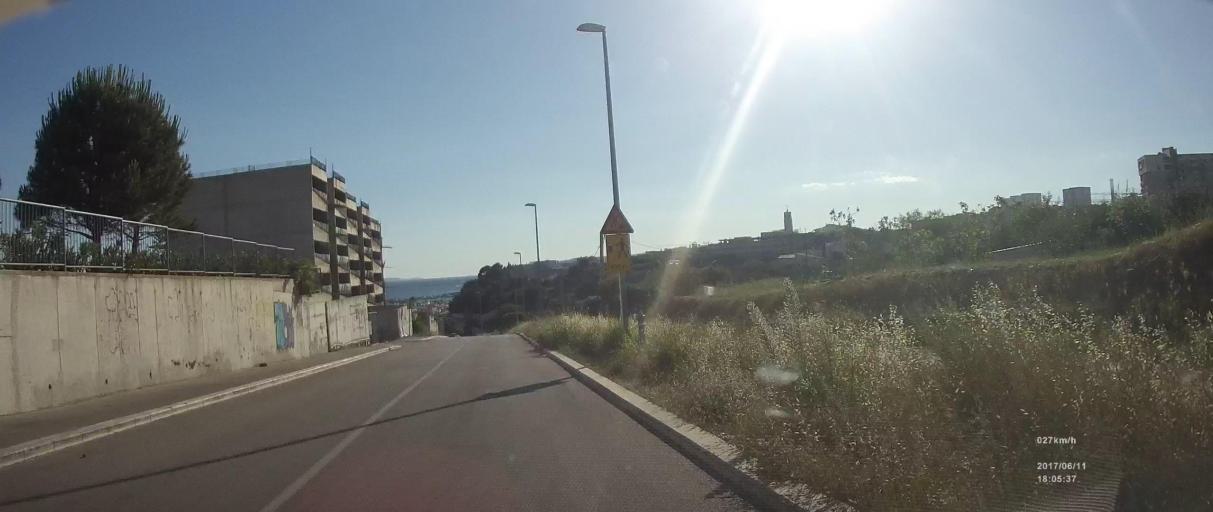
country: HR
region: Splitsko-Dalmatinska
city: Vranjic
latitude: 43.5034
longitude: 16.4695
